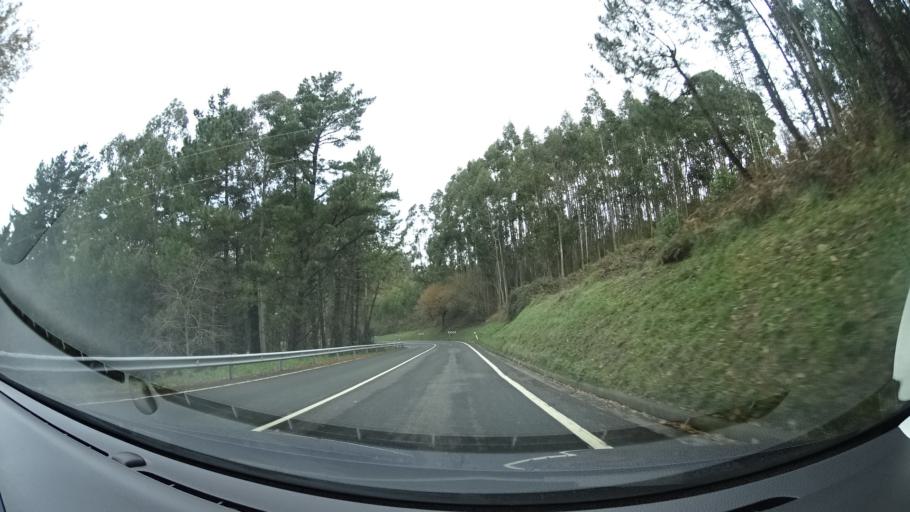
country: ES
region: Basque Country
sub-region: Bizkaia
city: Bakio
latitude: 43.3858
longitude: -2.7780
